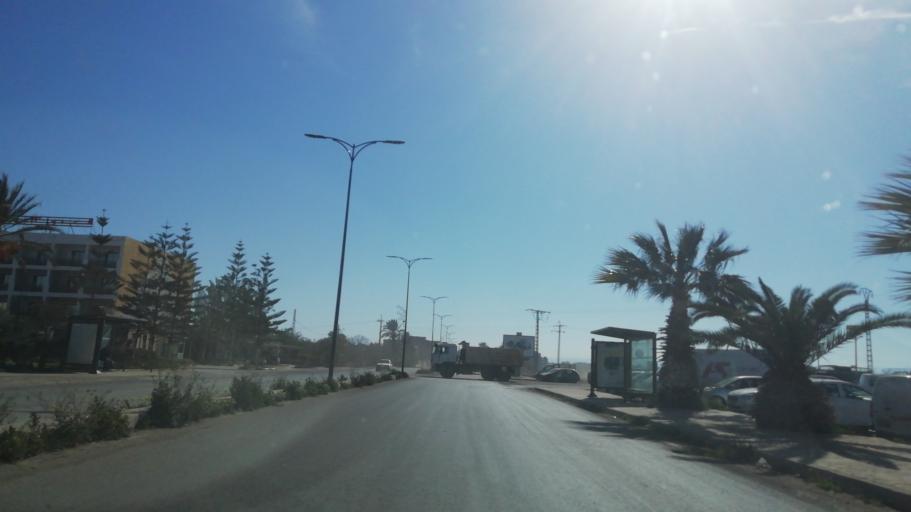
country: DZ
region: Oran
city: Es Senia
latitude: 35.6215
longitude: -0.5910
